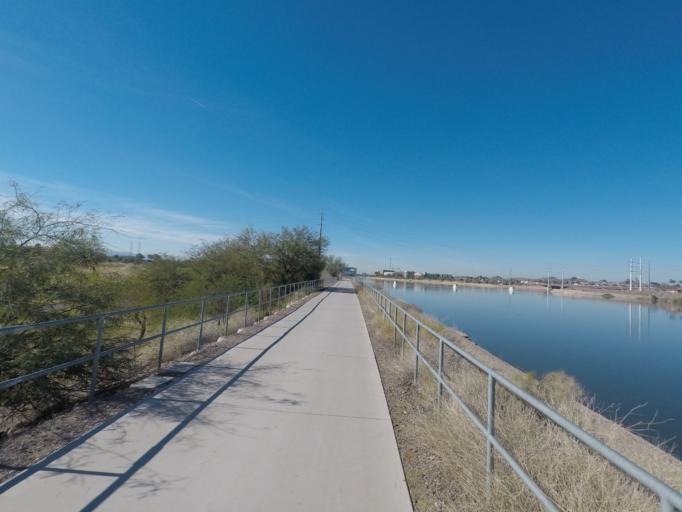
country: US
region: Arizona
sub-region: Maricopa County
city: Tempe
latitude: 33.4329
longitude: -111.9120
